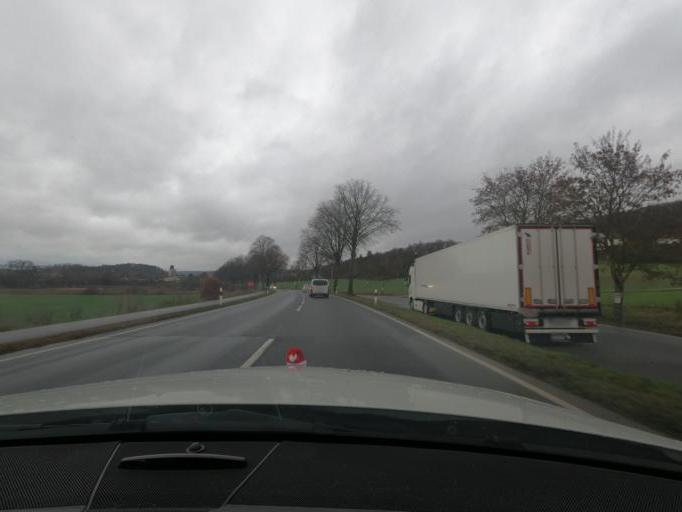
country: DE
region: Lower Saxony
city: Einbeck
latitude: 51.7915
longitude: 9.9318
